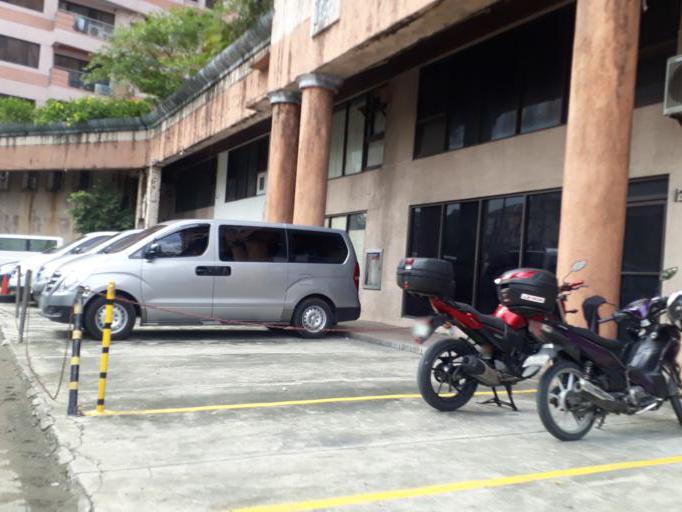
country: PH
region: Metro Manila
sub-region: San Juan
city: San Juan
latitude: 14.6104
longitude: 121.0339
